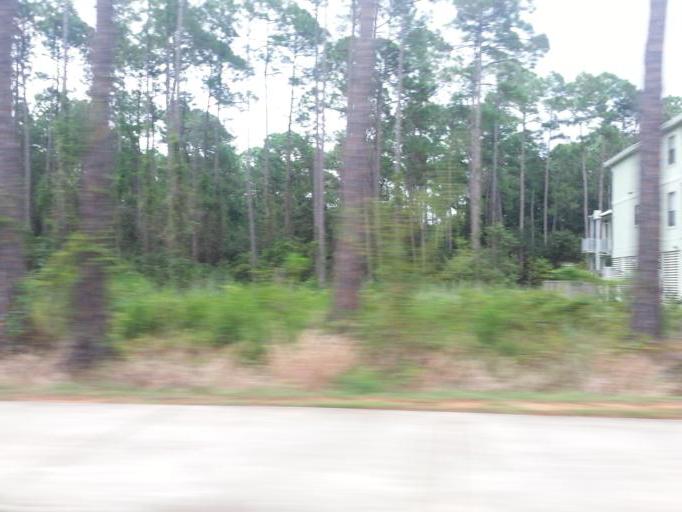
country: US
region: Alabama
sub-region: Baldwin County
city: Point Clear
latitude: 30.4292
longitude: -87.9102
